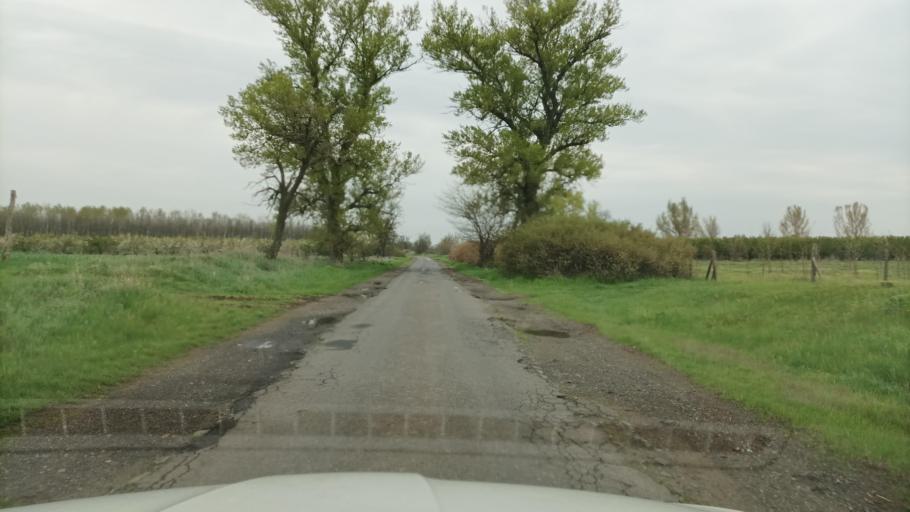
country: HU
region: Pest
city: Nagykoros
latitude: 46.9978
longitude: 19.8007
